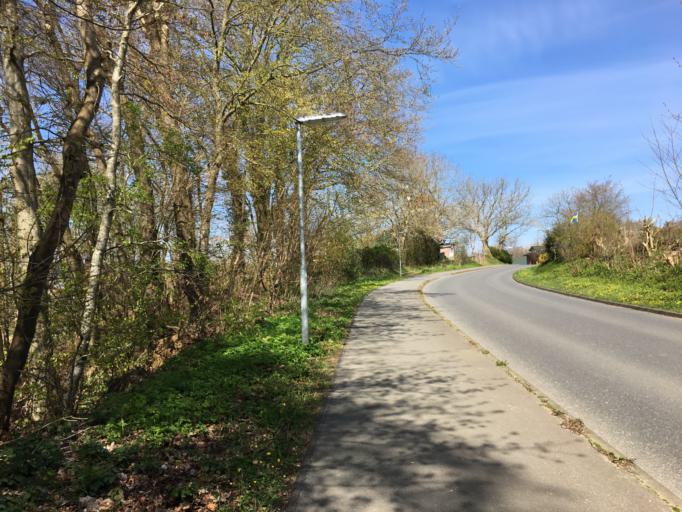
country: DE
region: Schleswig-Holstein
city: Dollrottfeld
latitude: 54.5914
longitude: 9.8039
